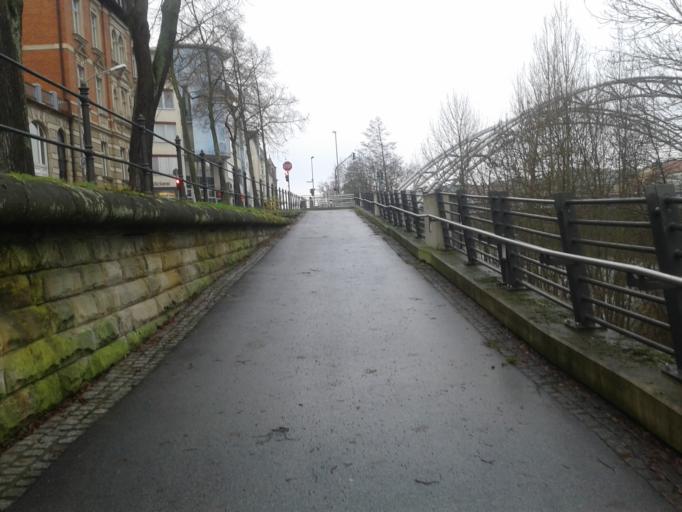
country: DE
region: Bavaria
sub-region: Upper Franconia
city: Bamberg
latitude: 49.8942
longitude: 10.8944
